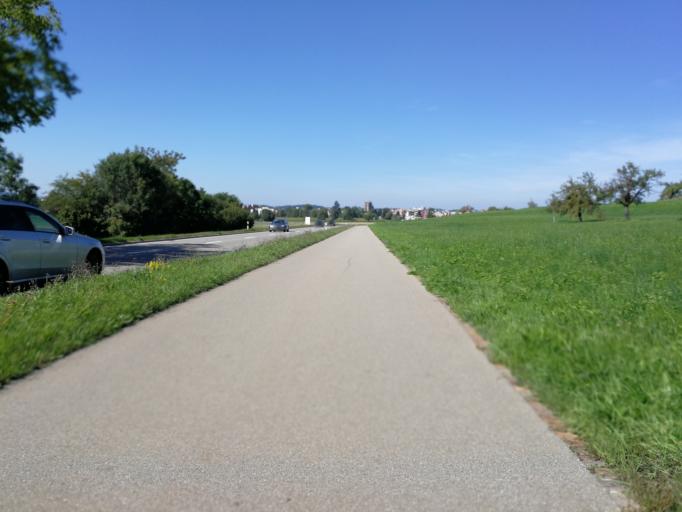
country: CH
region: Zurich
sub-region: Bezirk Hinwil
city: Wetzikon / Kempten
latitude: 47.3238
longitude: 8.8221
